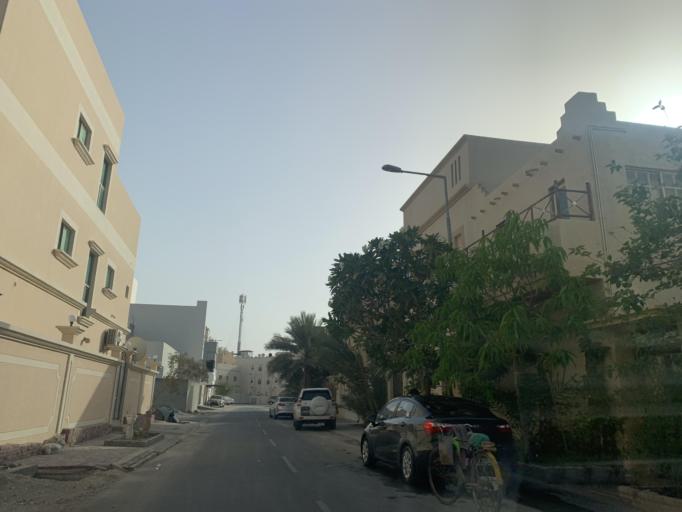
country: BH
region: Northern
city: Madinat `Isa
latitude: 26.1580
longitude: 50.5085
